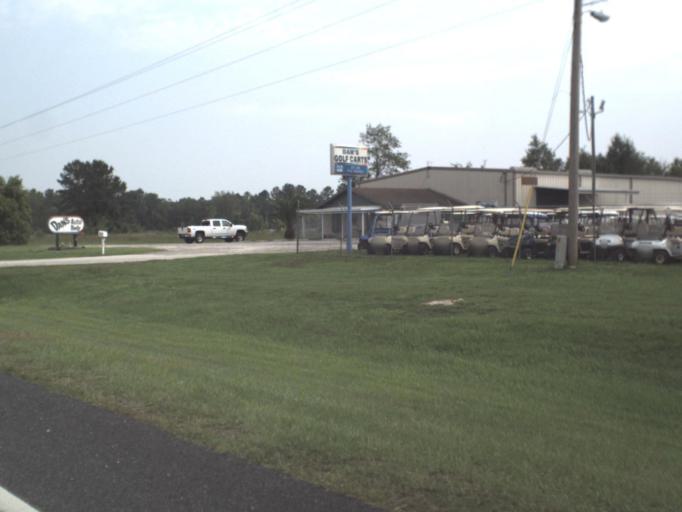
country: US
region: Florida
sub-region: Levy County
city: Williston
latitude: 29.3836
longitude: -82.4248
